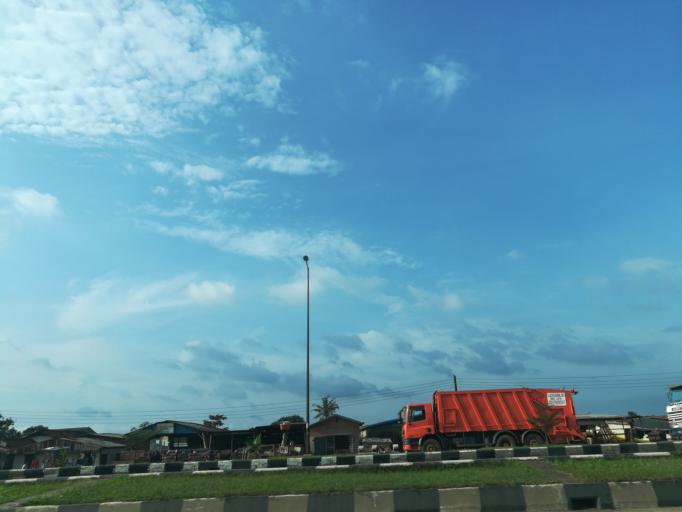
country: NG
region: Lagos
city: Ebute Ikorodu
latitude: 6.6089
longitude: 3.4352
